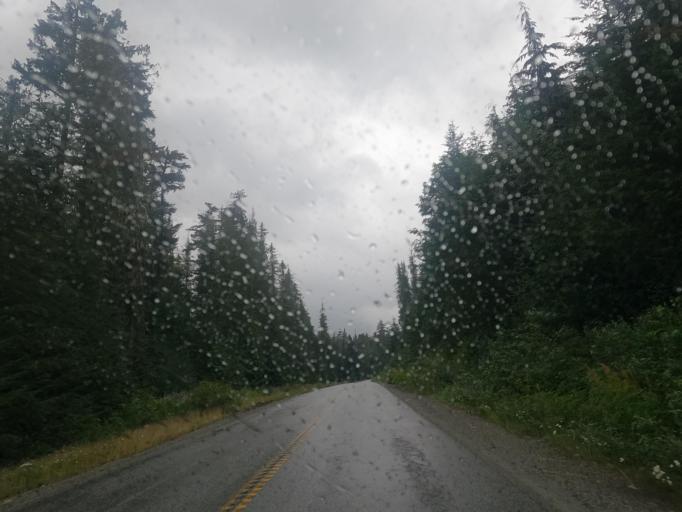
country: CA
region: British Columbia
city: Pemberton
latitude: 50.3394
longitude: -122.5401
